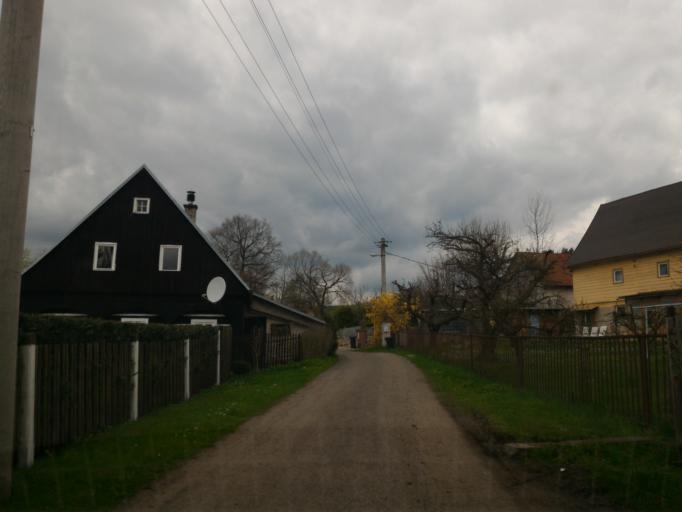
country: CZ
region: Ustecky
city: Varnsdorf
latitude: 50.9095
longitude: 14.6512
